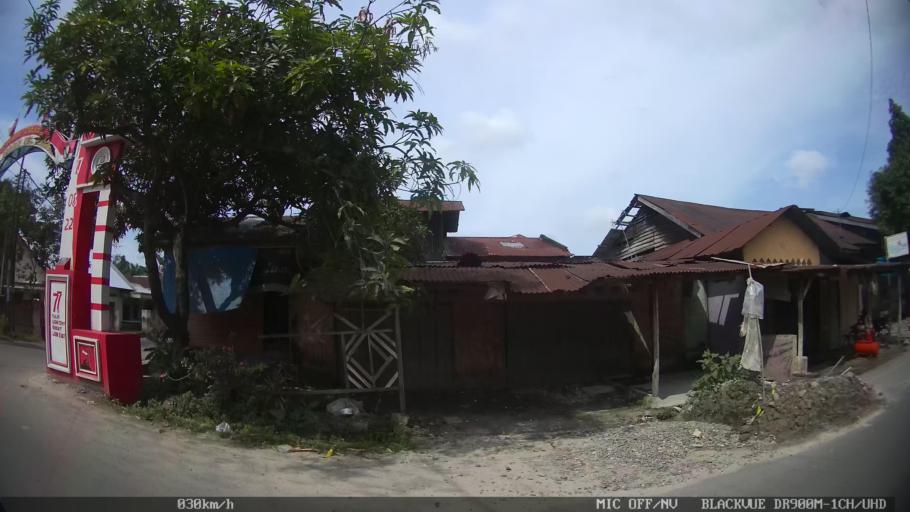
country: ID
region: North Sumatra
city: Percut
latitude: 3.6072
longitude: 98.8533
